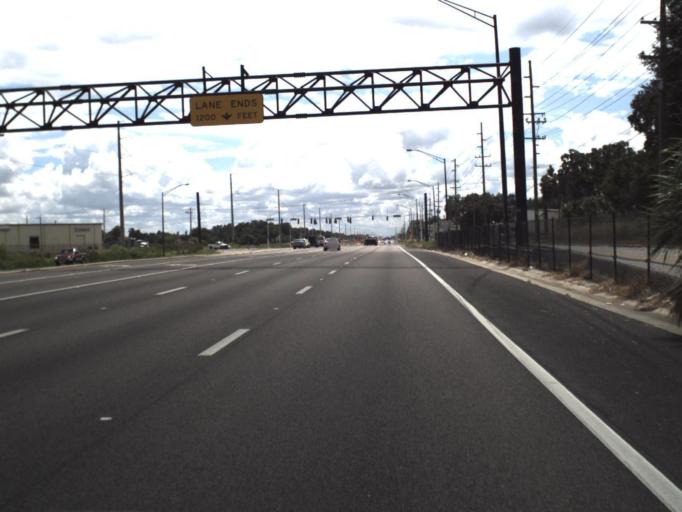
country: US
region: Florida
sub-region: Polk County
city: Crystal Lake
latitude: 27.9986
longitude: -81.9007
